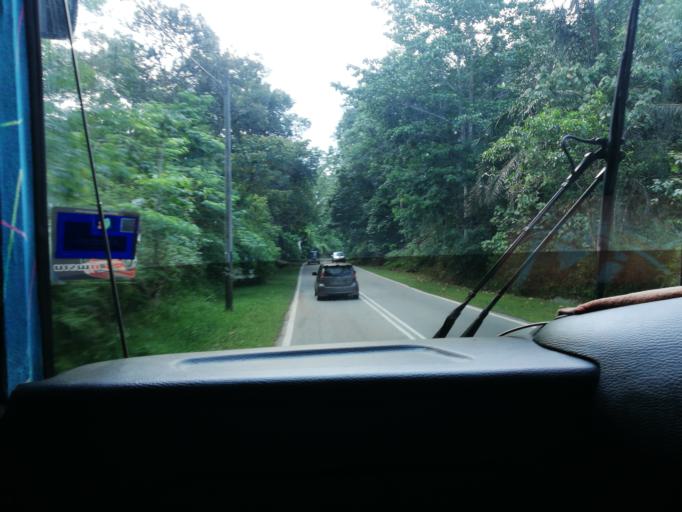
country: MY
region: Kedah
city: Kulim
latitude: 5.3037
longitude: 100.6183
